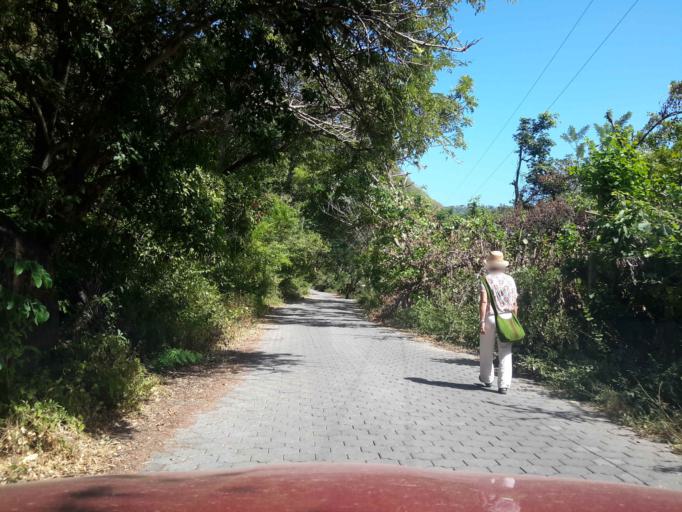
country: NI
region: Masaya
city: Catarina
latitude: 11.9410
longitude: -86.0478
